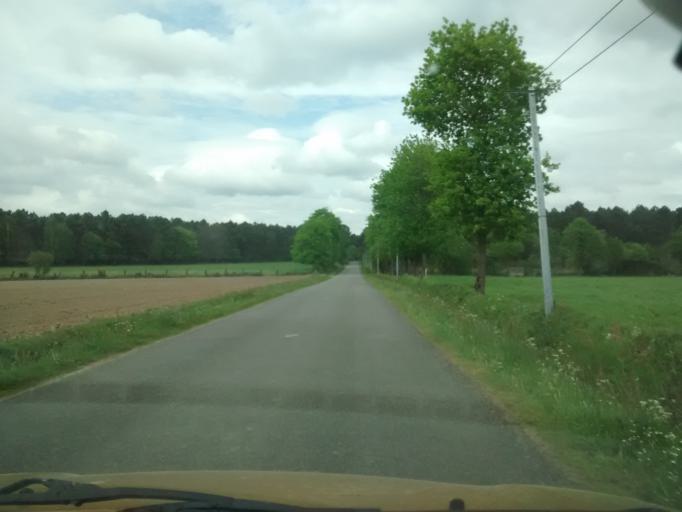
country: FR
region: Brittany
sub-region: Departement du Morbihan
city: Molac
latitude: 47.7334
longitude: -2.4233
